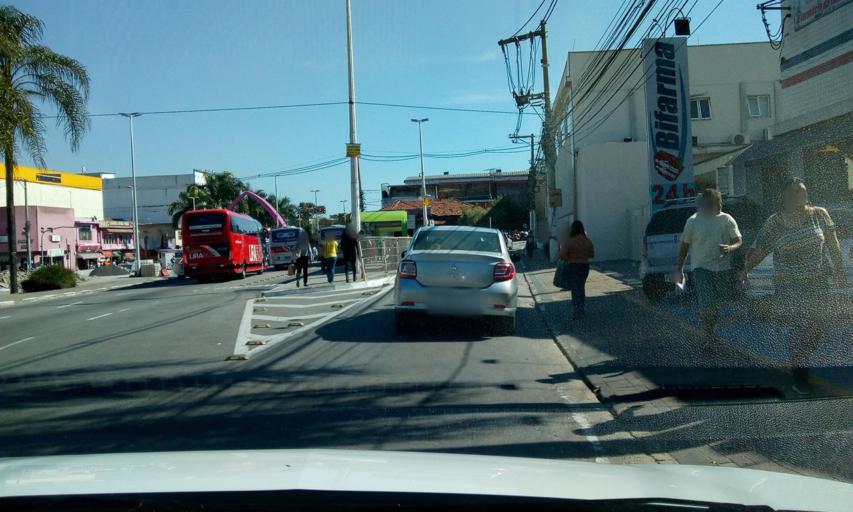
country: BR
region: Sao Paulo
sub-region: Barueri
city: Barueri
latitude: -23.5109
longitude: -46.8742
